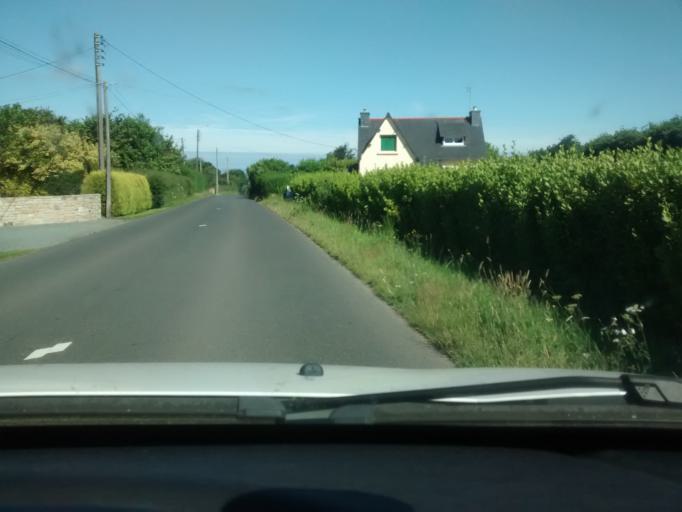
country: FR
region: Brittany
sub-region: Departement des Cotes-d'Armor
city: Trevou-Treguignec
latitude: 48.8112
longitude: -3.3321
